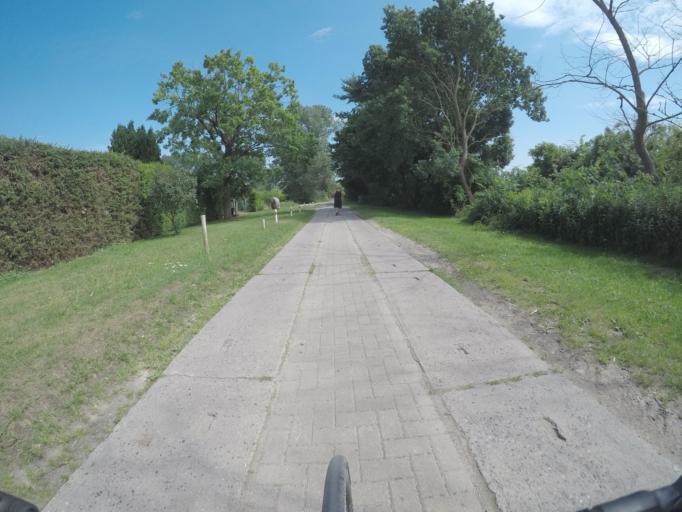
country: DE
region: Mecklenburg-Vorpommern
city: Rambin
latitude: 54.3576
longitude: 13.1937
